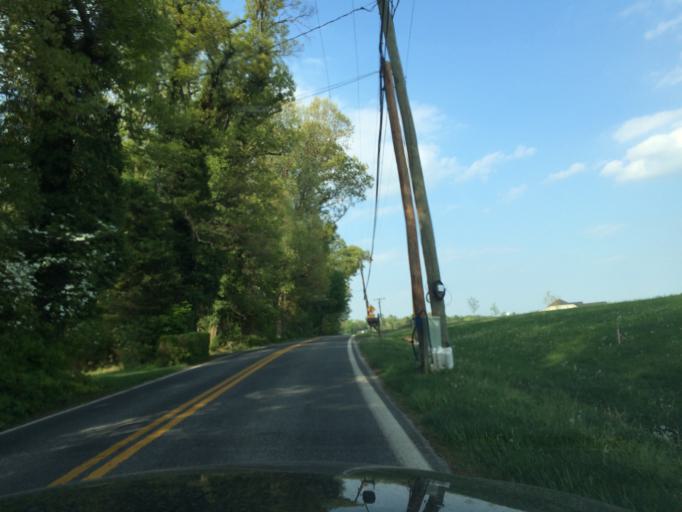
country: US
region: Maryland
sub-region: Howard County
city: Highland
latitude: 39.2537
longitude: -77.0193
